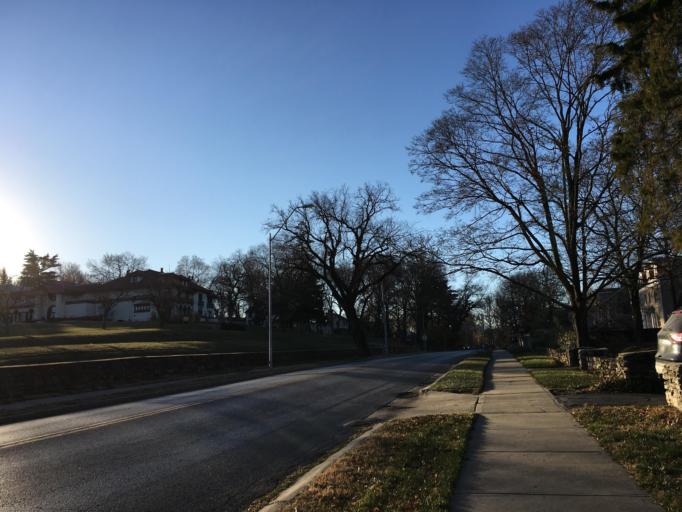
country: US
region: Kansas
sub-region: Johnson County
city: Westwood
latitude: 39.0318
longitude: -94.5830
